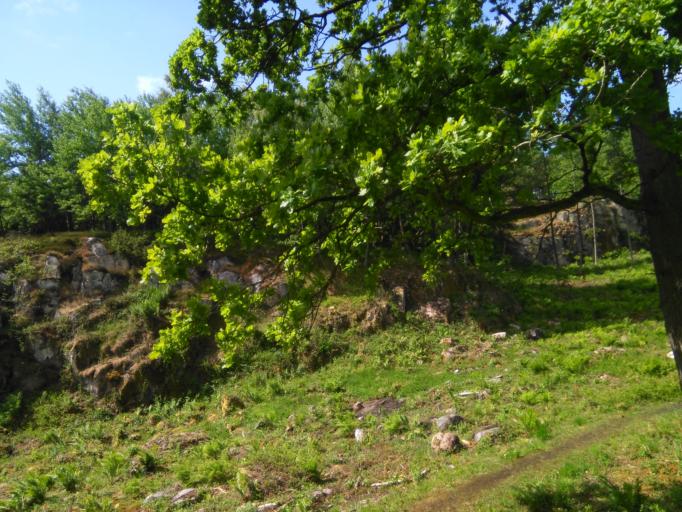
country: DK
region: Capital Region
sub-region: Bornholm Kommune
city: Nexo
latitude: 55.0911
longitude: 15.1057
